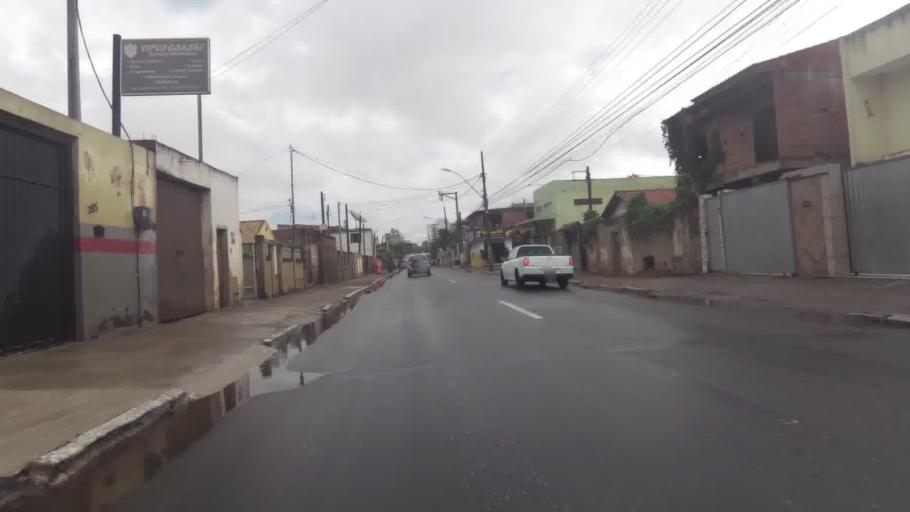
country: BR
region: Rio de Janeiro
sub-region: Campos Dos Goytacazes
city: Campos
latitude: -21.7472
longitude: -41.3360
